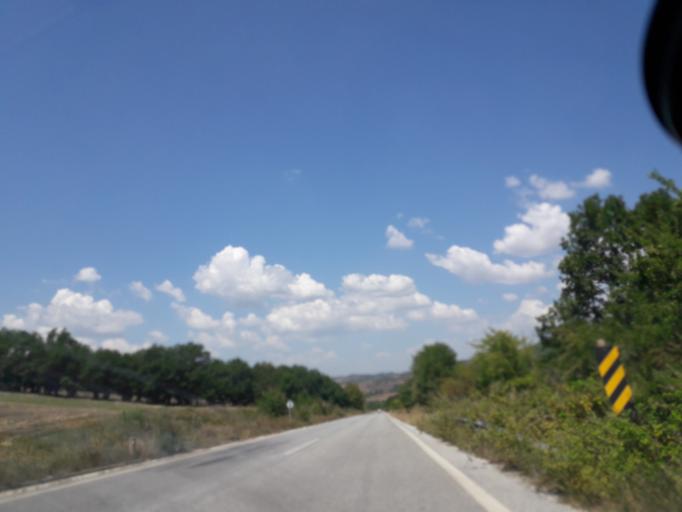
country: GR
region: Central Macedonia
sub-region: Nomos Chalkidikis
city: Polygyros
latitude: 40.4573
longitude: 23.4038
